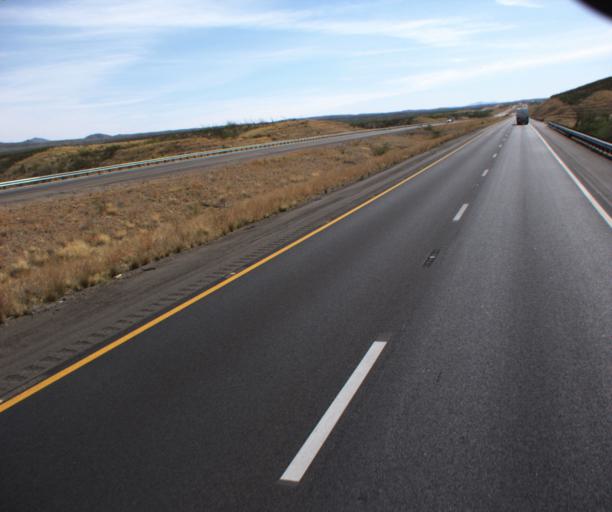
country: US
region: Arizona
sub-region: Cochise County
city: Mescal
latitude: 31.9869
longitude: -110.5790
